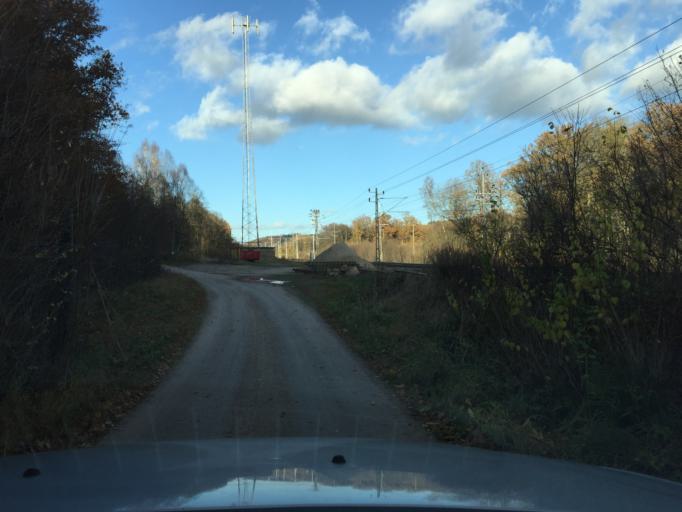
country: SE
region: Skane
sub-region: Hassleholms Kommun
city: Tormestorp
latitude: 56.0740
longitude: 13.7365
